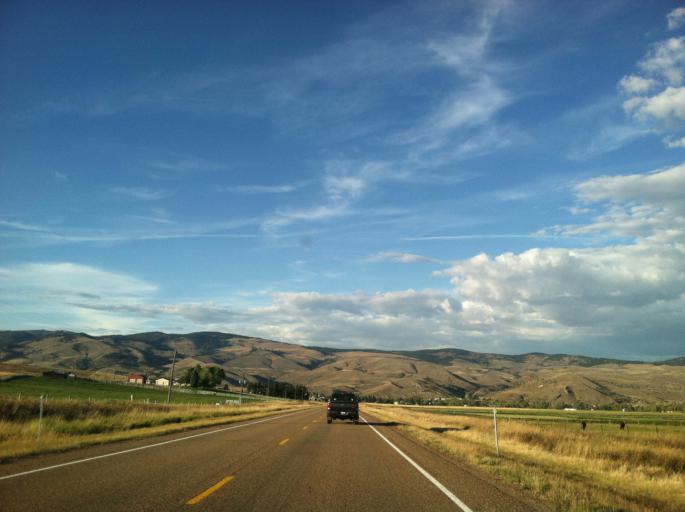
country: US
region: Montana
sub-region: Granite County
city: Philipsburg
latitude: 46.6464
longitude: -113.1638
